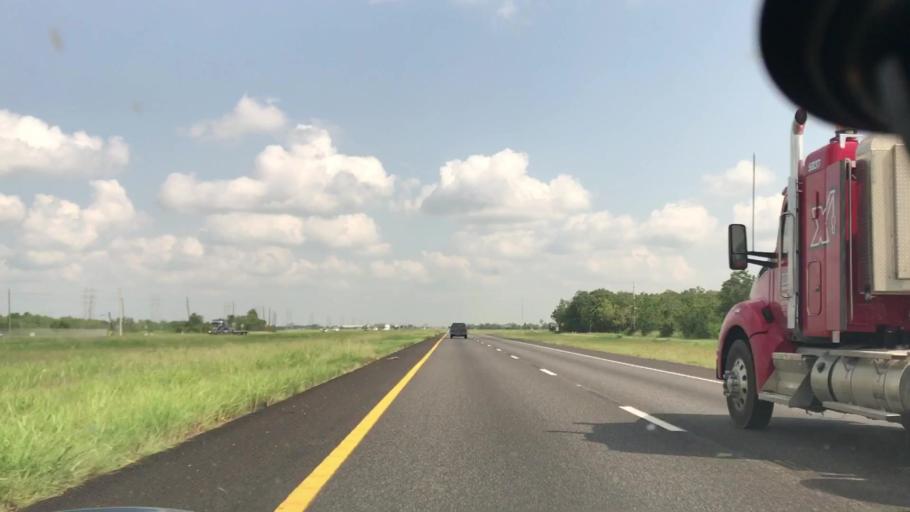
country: US
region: Texas
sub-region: Brazoria County
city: Rosharon
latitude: 29.4029
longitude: -95.4268
